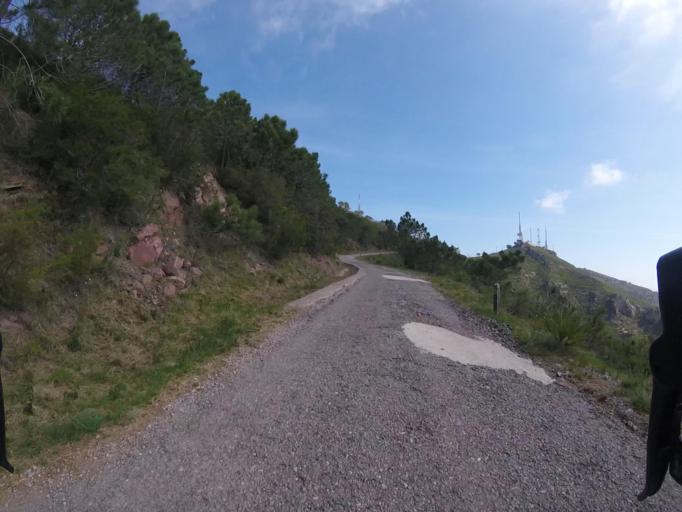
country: ES
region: Valencia
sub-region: Provincia de Castello
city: Benicassim
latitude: 40.0822
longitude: 0.0252
